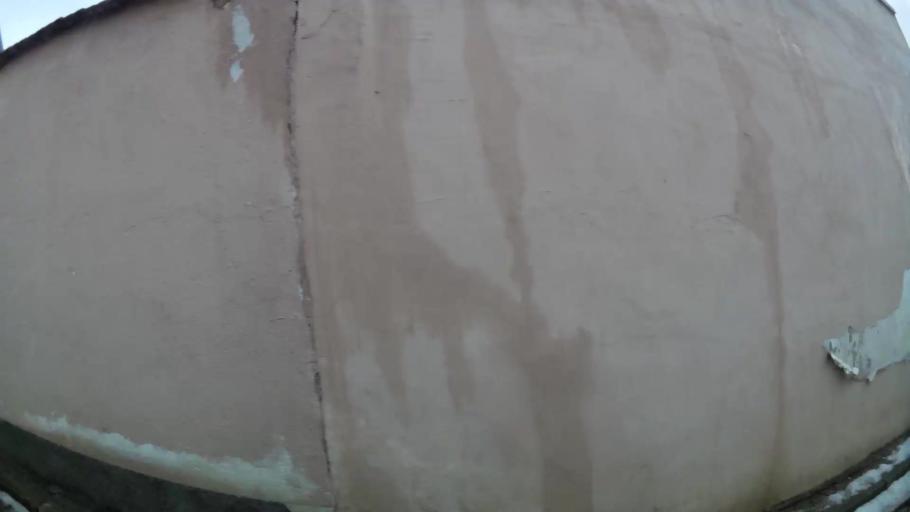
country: XK
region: Pristina
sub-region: Komuna e Prishtines
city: Pristina
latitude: 42.6733
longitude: 21.1621
